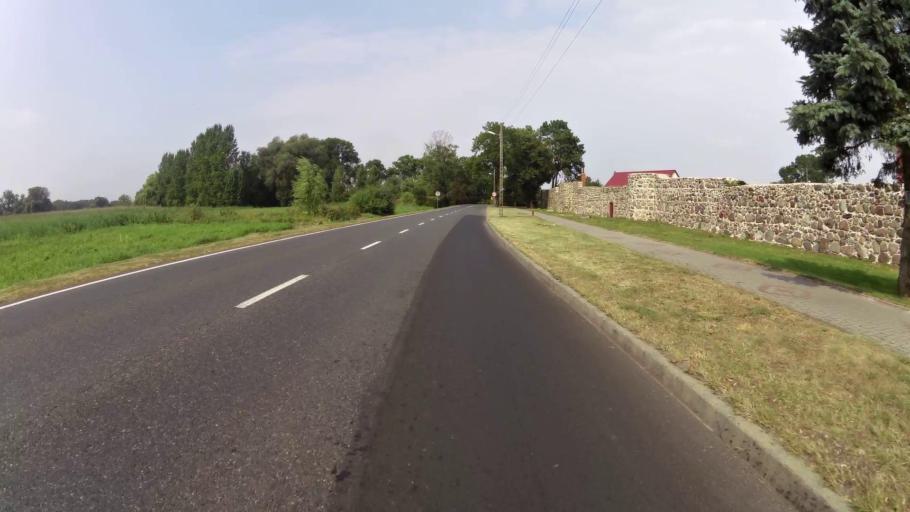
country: PL
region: West Pomeranian Voivodeship
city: Trzcinsko Zdroj
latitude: 52.9628
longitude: 14.6074
